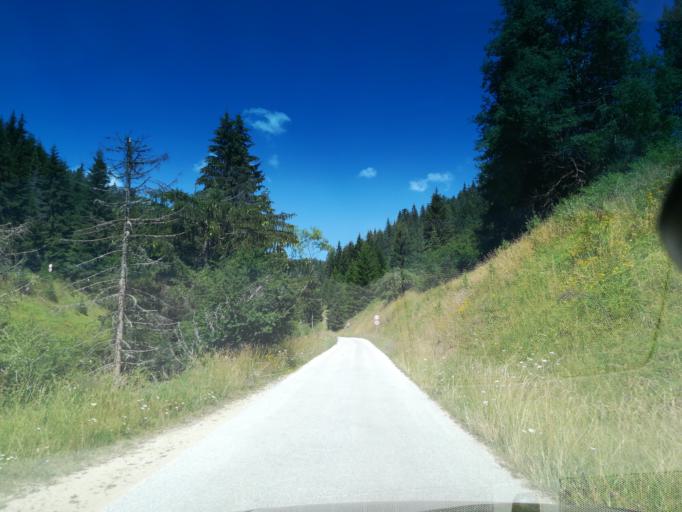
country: BG
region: Smolyan
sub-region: Obshtina Chepelare
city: Chepelare
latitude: 41.6735
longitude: 24.7907
